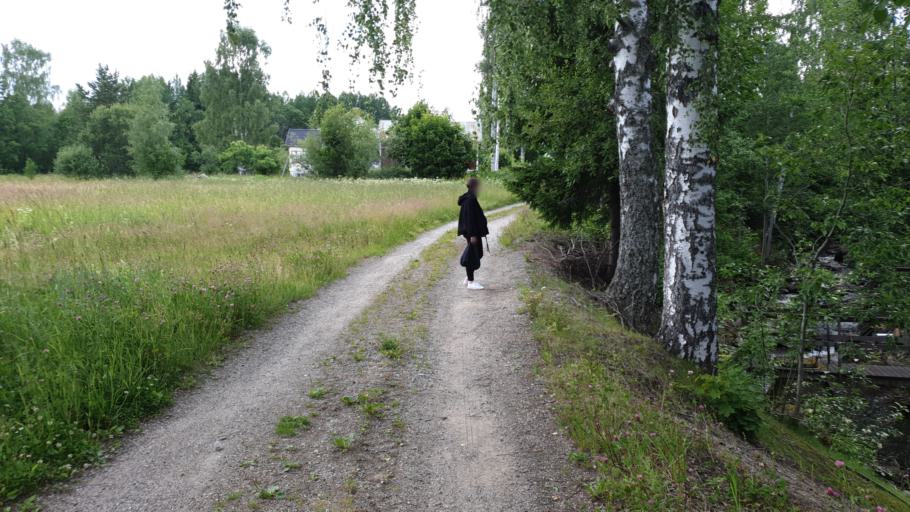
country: SE
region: Gaevleborg
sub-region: Nordanstigs Kommun
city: Bergsjoe
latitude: 62.0399
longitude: 17.0896
